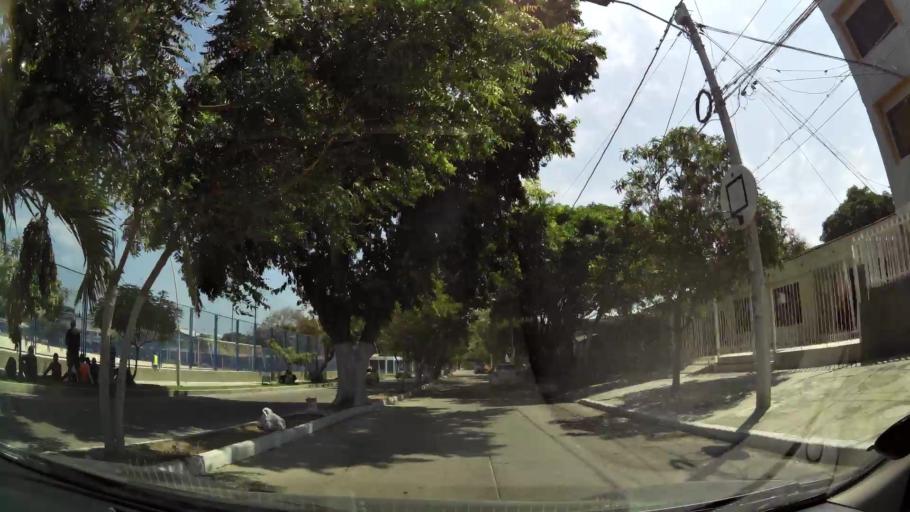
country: CO
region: Atlantico
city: Barranquilla
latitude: 10.9661
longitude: -74.7996
